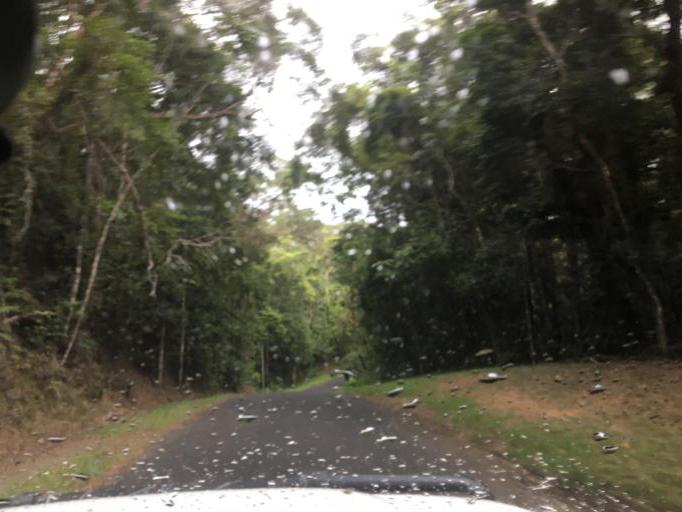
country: AU
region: Queensland
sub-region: Tablelands
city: Kuranda
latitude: -16.8426
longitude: 145.6426
